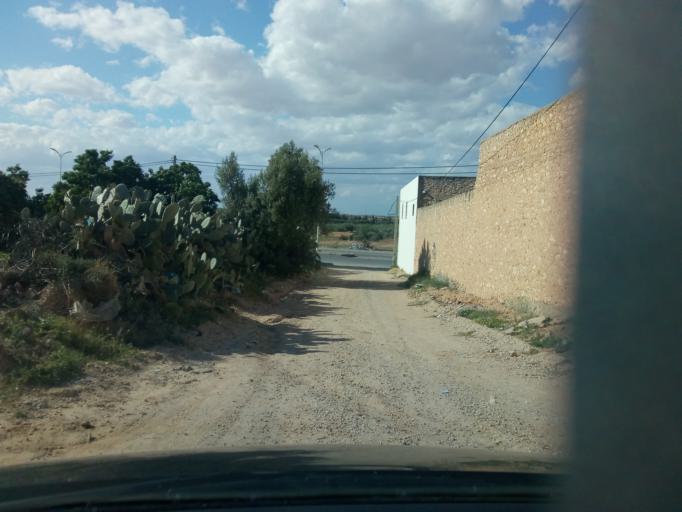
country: TN
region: Safaqis
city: Sfax
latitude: 34.7311
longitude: 10.6019
